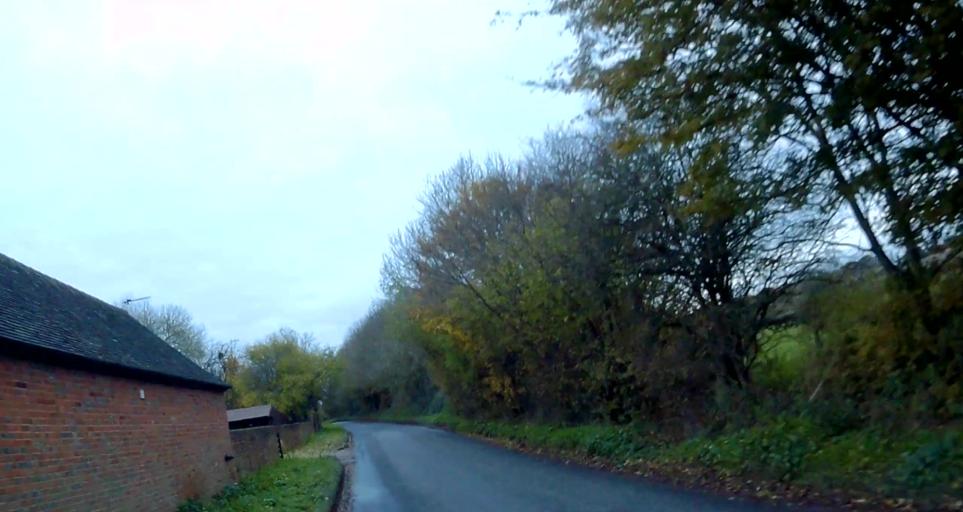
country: GB
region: England
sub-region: Hampshire
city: Odiham
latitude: 51.2385
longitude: -0.9855
